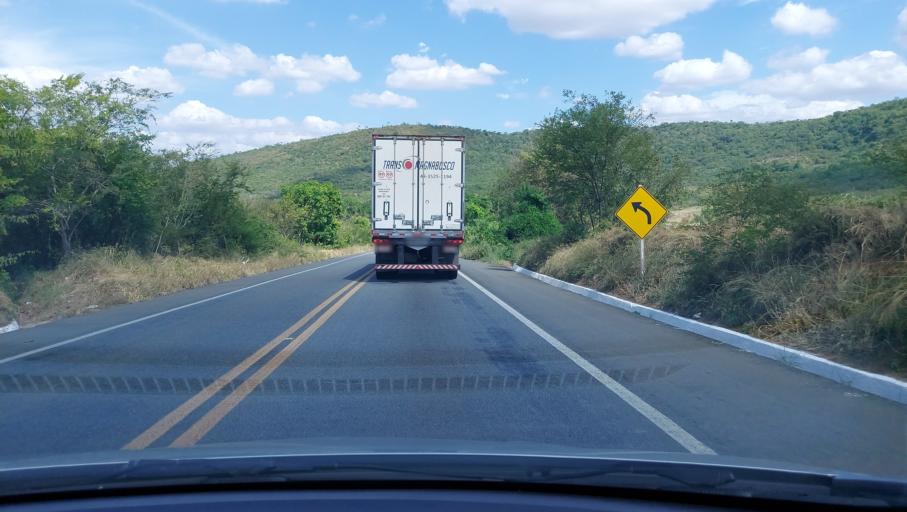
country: BR
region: Bahia
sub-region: Itaberaba
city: Itaberaba
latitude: -12.5296
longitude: -40.3508
